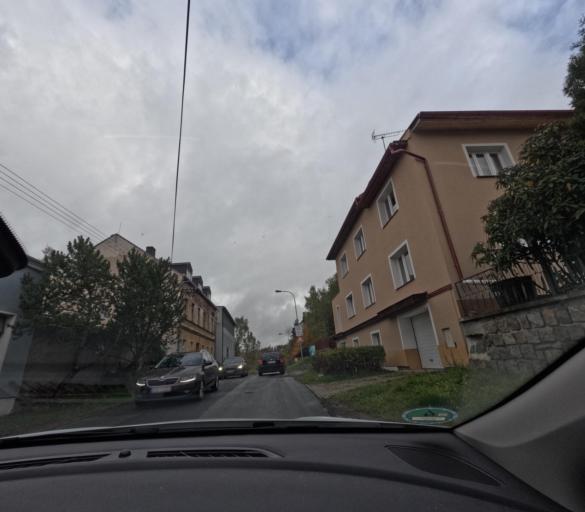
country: CZ
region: Karlovarsky
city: Dalovice
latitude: 50.2145
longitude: 12.9040
